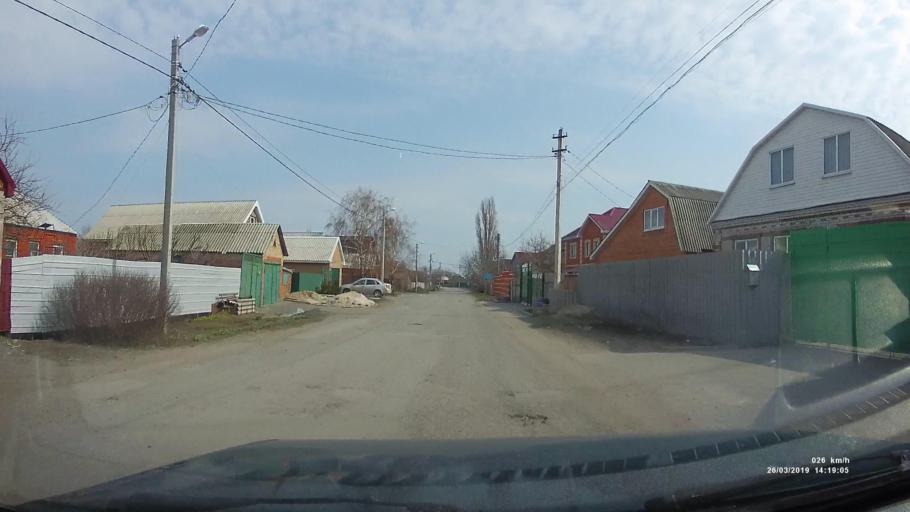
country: RU
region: Rostov
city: Novobessergenovka
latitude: 47.1899
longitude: 38.8675
